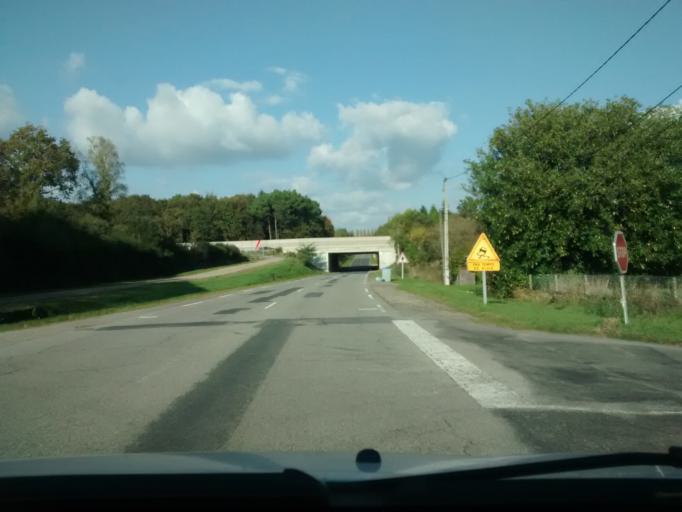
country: FR
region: Pays de la Loire
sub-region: Departement de la Loire-Atlantique
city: Sautron
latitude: 47.2555
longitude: -1.6902
